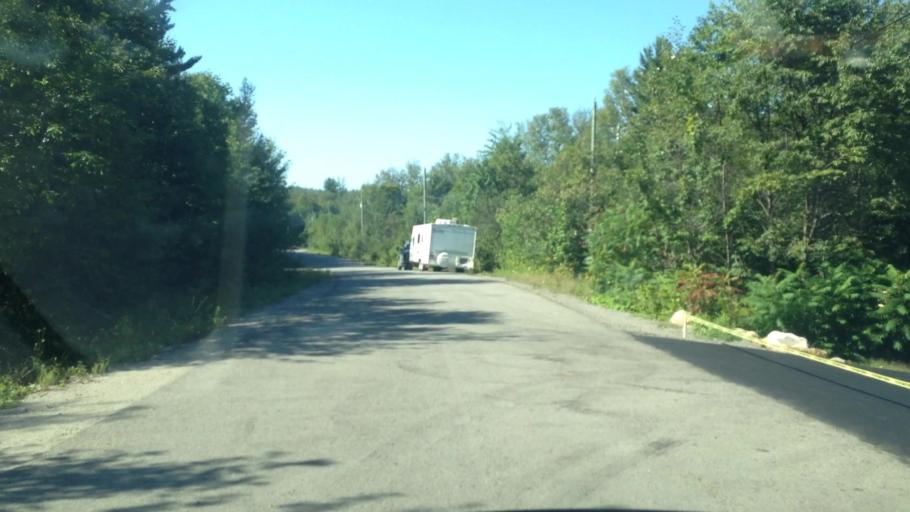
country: CA
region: Quebec
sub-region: Laurentides
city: Prevost
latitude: 45.8681
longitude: -74.0166
